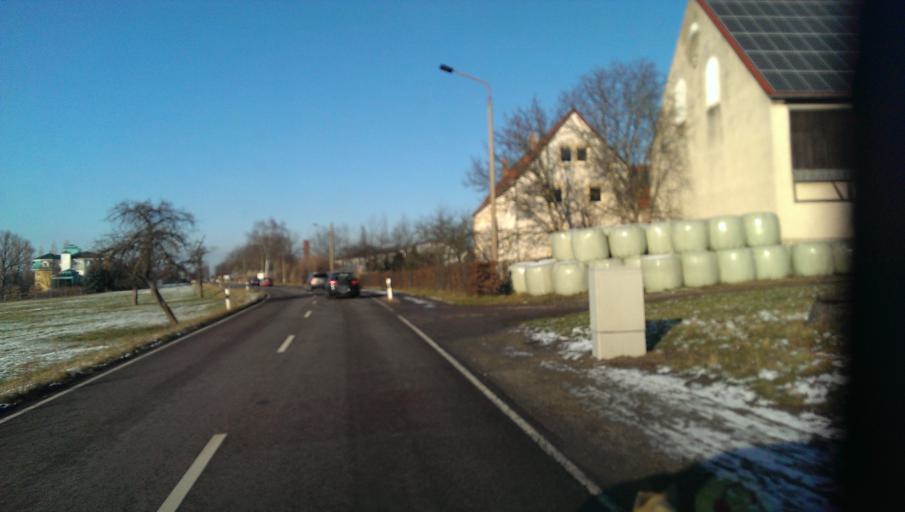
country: DE
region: Saxony
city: Wilsdruff
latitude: 51.0367
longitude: 13.5468
